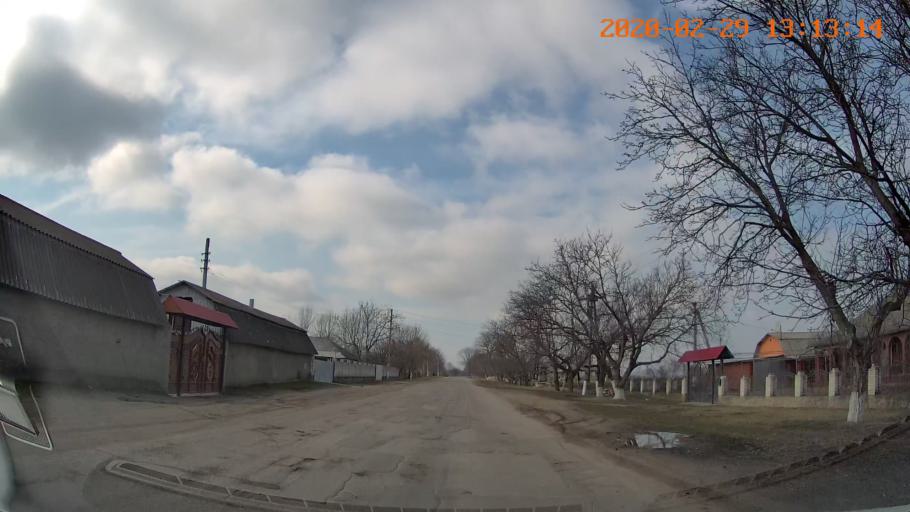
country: MD
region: Telenesti
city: Camenca
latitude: 48.0140
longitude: 28.6865
